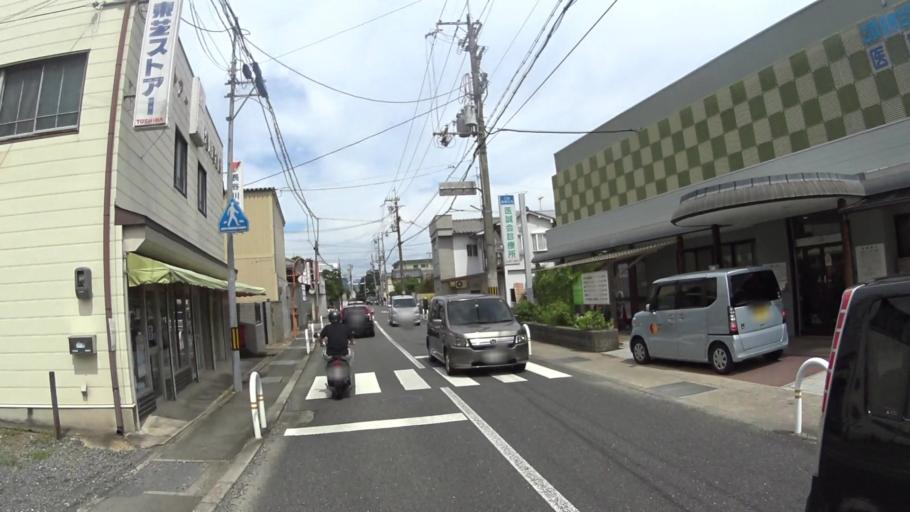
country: JP
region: Kyoto
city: Muko
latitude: 34.9504
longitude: 135.6990
